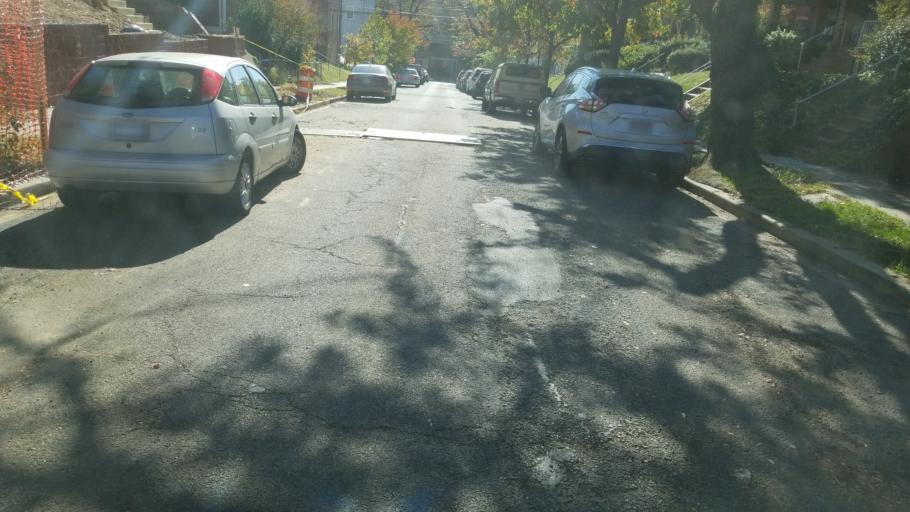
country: US
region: Maryland
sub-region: Prince George's County
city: Capitol Heights
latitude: 38.8913
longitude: -76.9358
